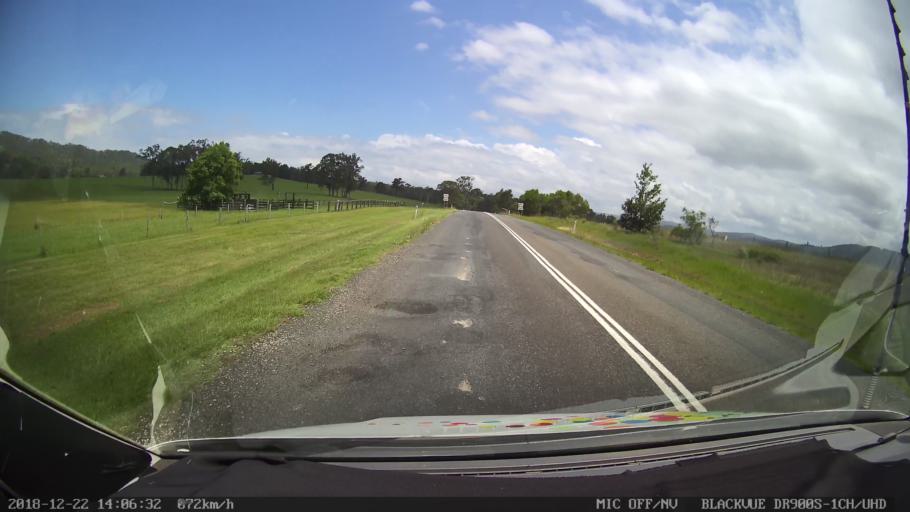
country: AU
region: New South Wales
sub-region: Clarence Valley
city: Coutts Crossing
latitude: -29.9565
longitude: 152.7276
